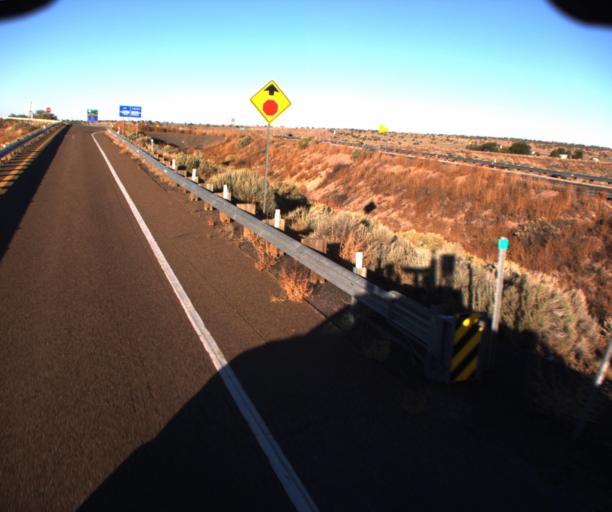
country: US
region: Arizona
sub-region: Apache County
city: Houck
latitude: 35.1911
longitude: -109.4345
